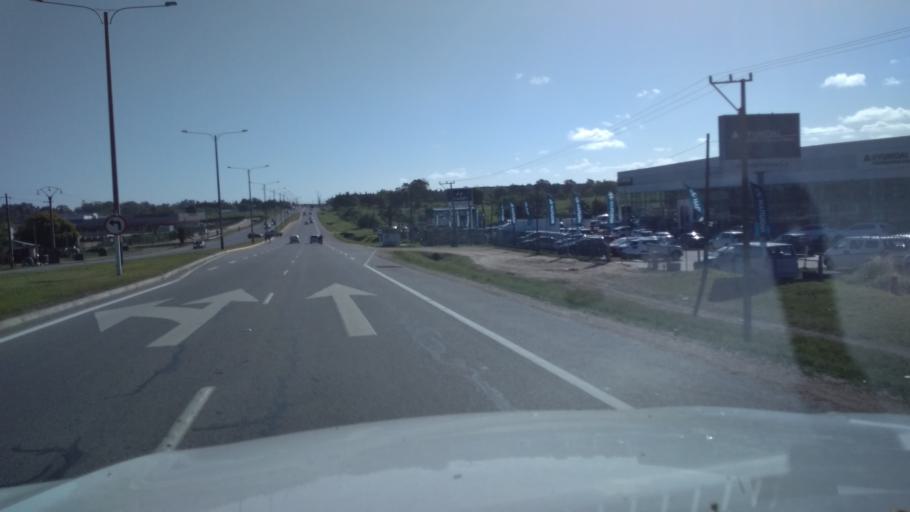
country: UY
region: Canelones
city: Colonia Nicolich
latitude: -34.8237
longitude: -55.9945
